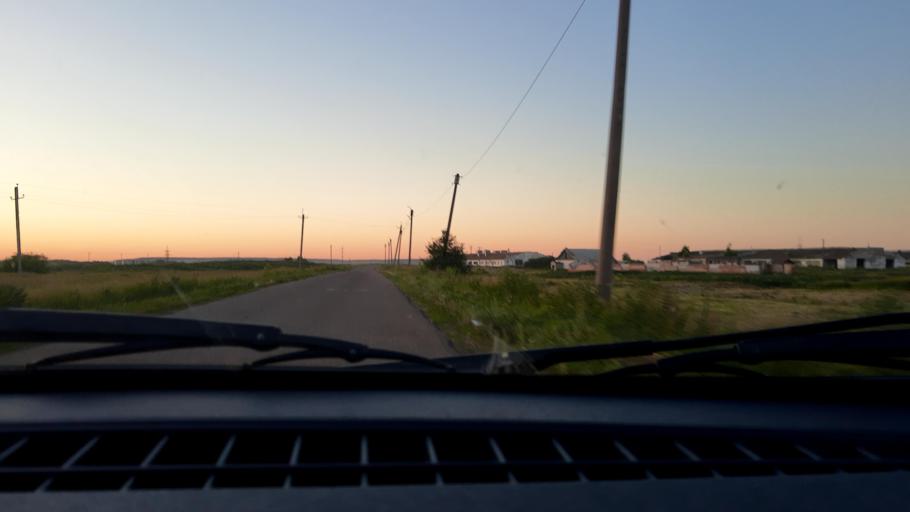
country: RU
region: Bashkortostan
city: Asanovo
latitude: 54.8952
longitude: 55.6256
